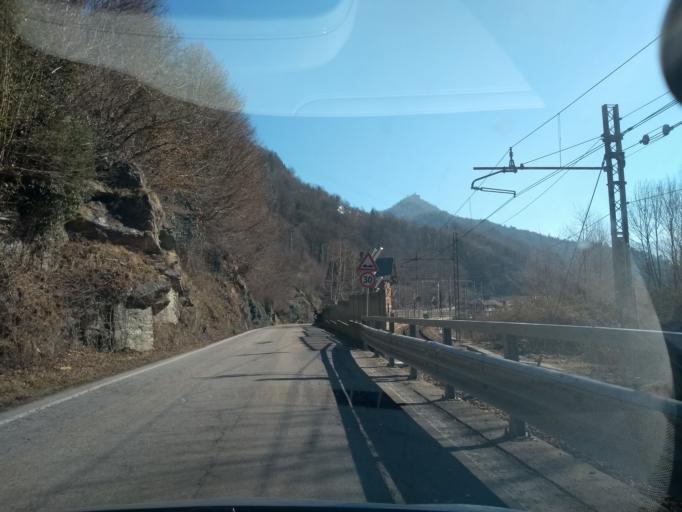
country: IT
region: Piedmont
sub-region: Provincia di Torino
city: Pessinetto
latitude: 45.2835
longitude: 7.4177
